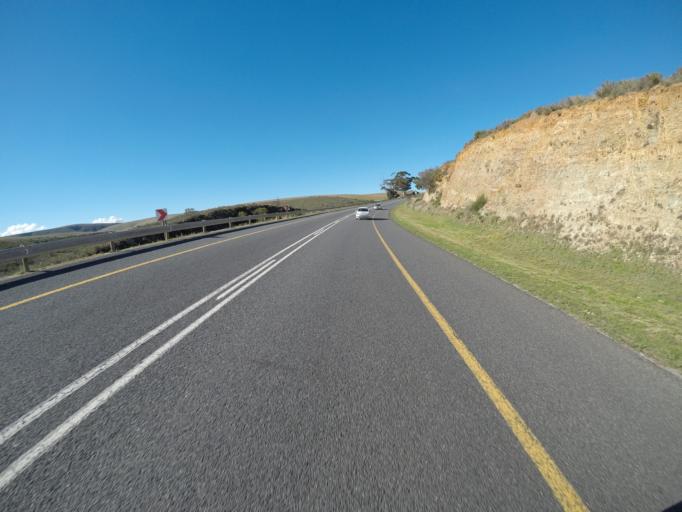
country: ZA
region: Western Cape
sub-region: Overberg District Municipality
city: Caledon
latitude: -34.2318
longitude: 19.2397
